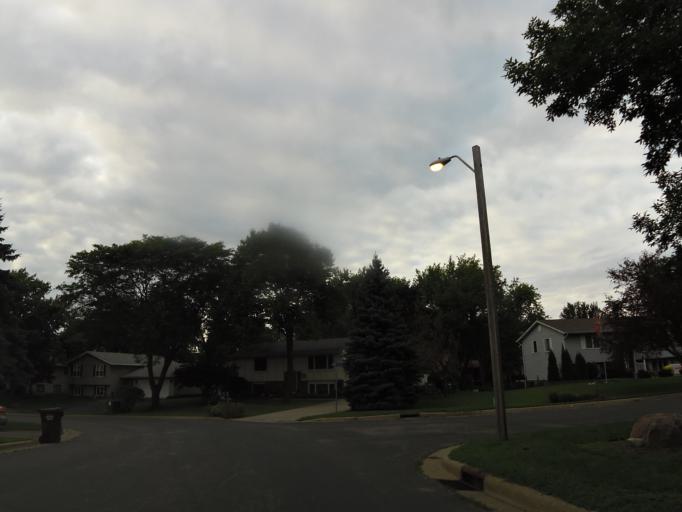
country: US
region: Minnesota
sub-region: Scott County
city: Prior Lake
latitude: 44.7077
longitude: -93.4218
